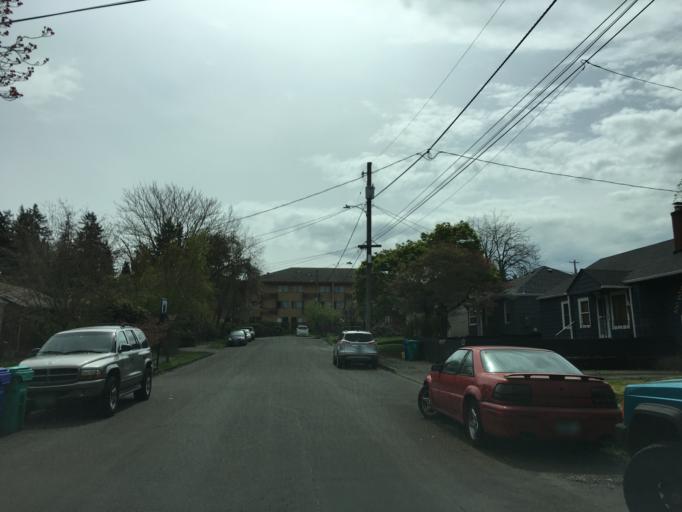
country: US
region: Oregon
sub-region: Multnomah County
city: Lents
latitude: 45.5549
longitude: -122.5776
